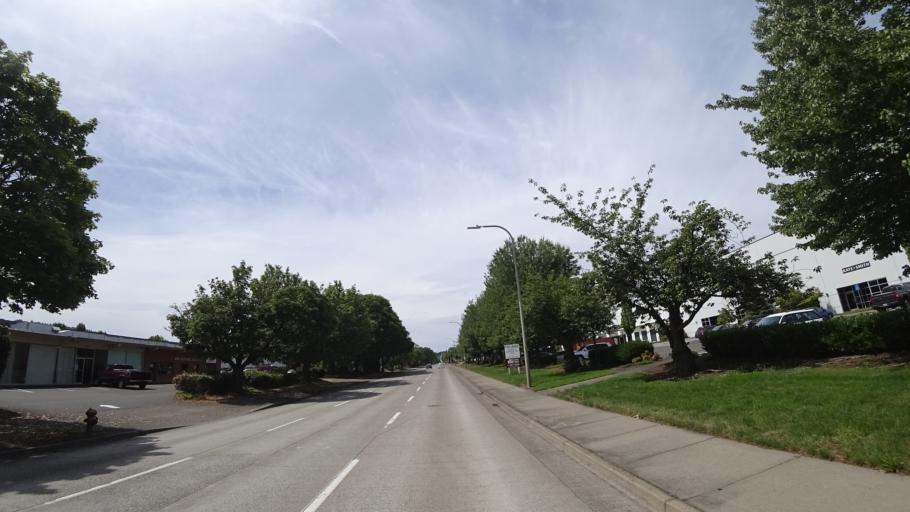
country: US
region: Oregon
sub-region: Multnomah County
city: Portland
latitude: 45.5586
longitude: -122.7043
